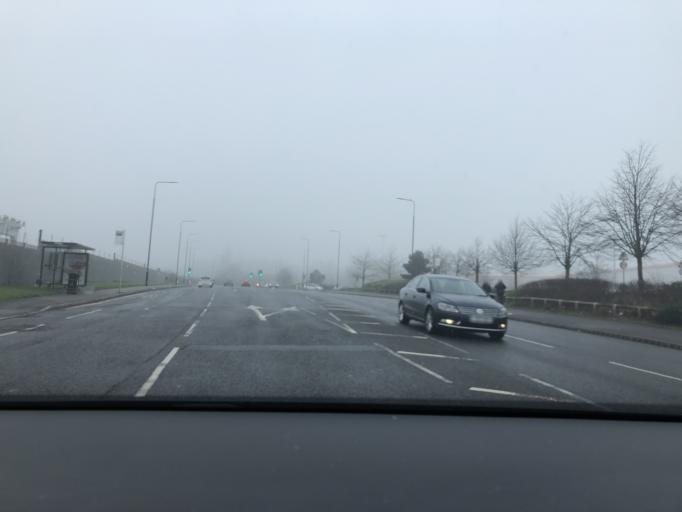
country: GB
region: England
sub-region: City and Borough of Salford
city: Eccles
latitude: 53.4708
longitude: -2.3500
